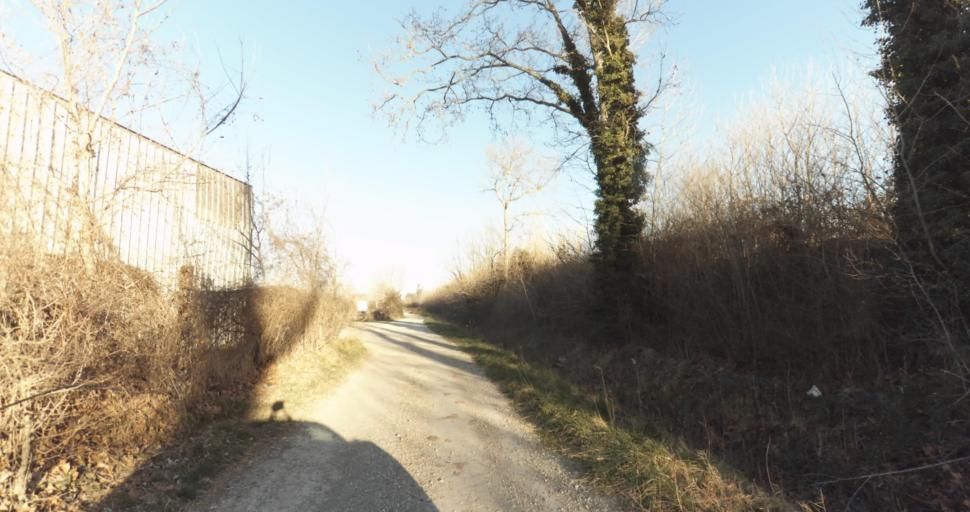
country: FR
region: Provence-Alpes-Cote d'Azur
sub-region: Departement des Bouches-du-Rhone
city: Barbentane
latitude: 43.9135
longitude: 4.7603
